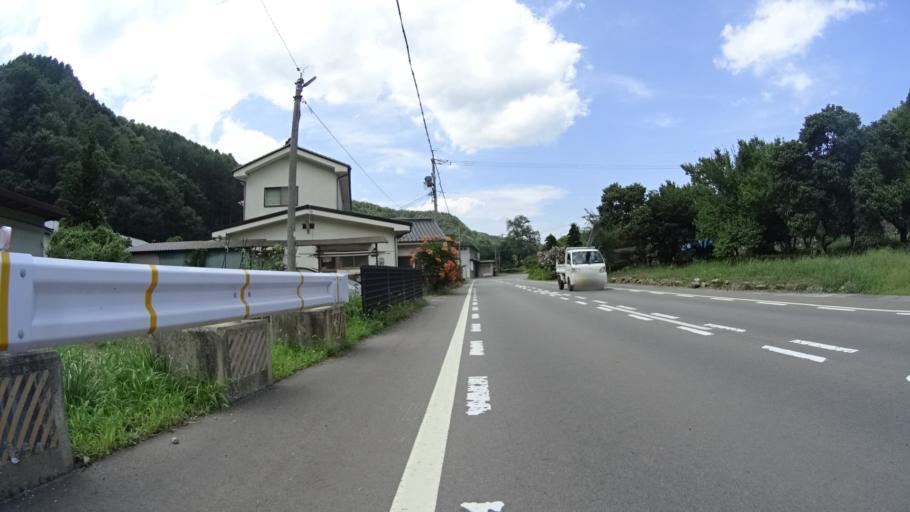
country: JP
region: Nagano
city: Saku
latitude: 36.0666
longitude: 138.5009
